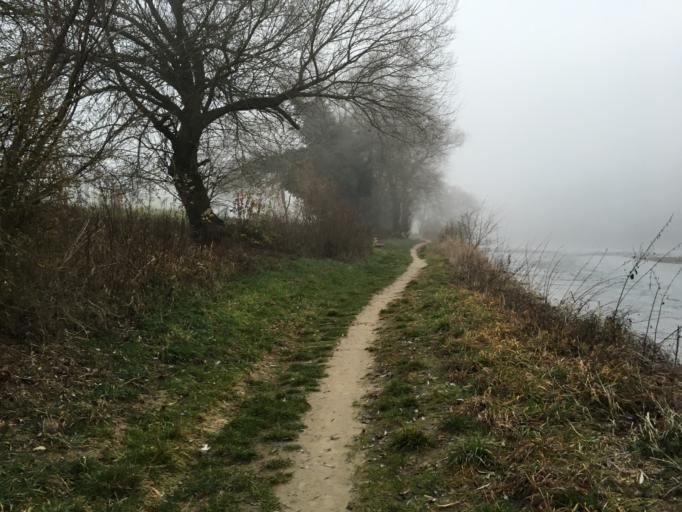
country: CH
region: Aargau
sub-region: Bezirk Zurzach
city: Bad Zurzach
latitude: 47.5919
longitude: 8.2977
